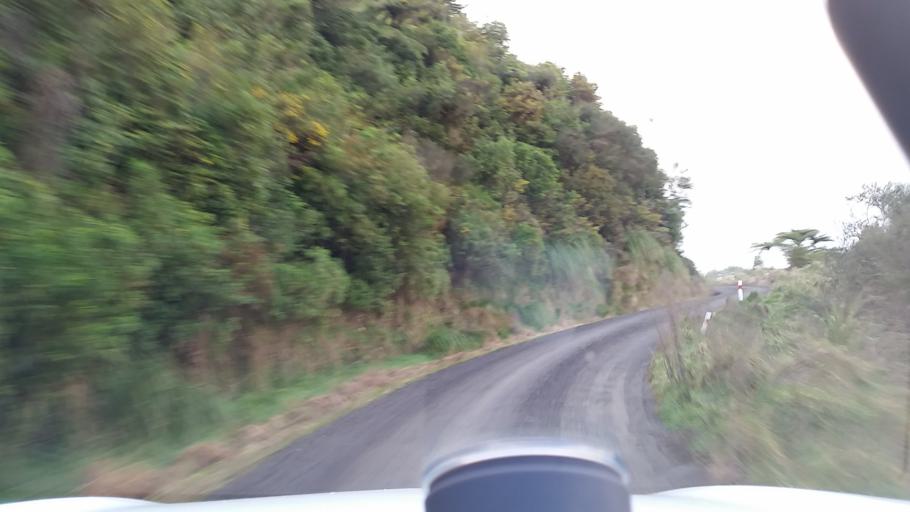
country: NZ
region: Taranaki
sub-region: South Taranaki District
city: Eltham
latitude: -39.4492
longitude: 174.4560
